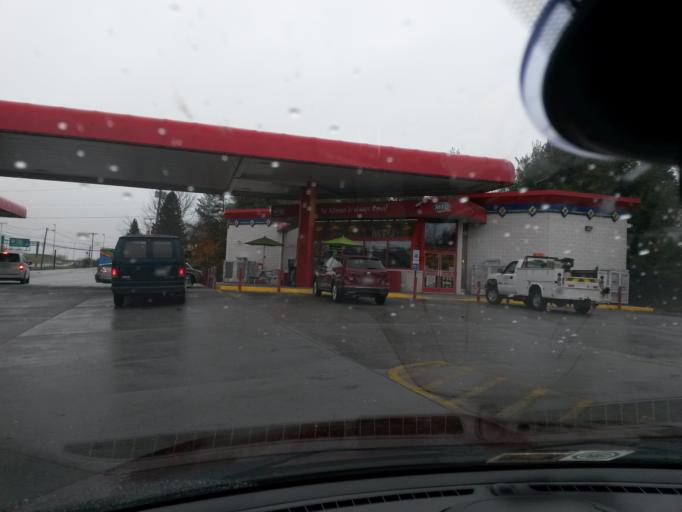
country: US
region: Virginia
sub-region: Montgomery County
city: Christiansburg
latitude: 37.1575
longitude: -80.4189
